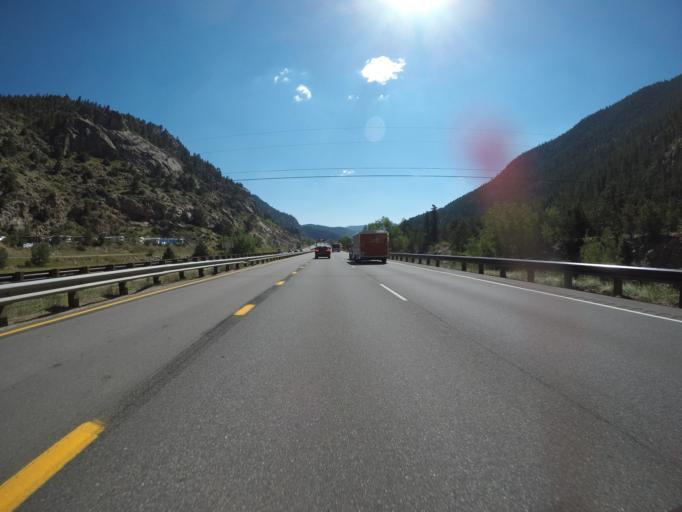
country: US
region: Colorado
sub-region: Clear Creek County
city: Georgetown
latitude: 39.7627
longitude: -105.6416
